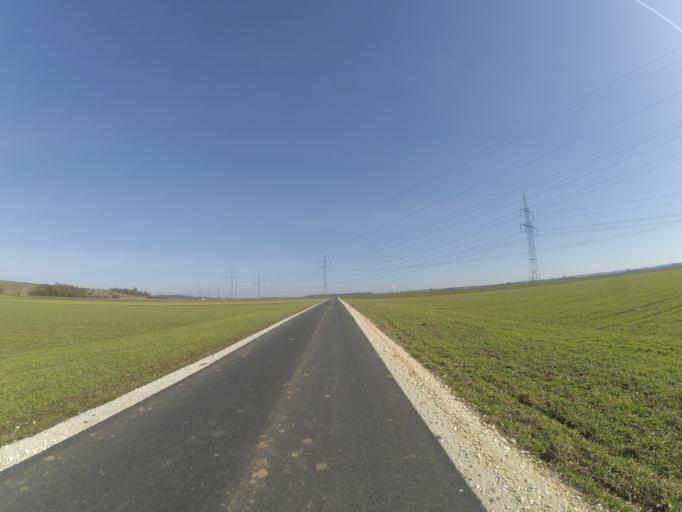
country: DE
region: Baden-Wuerttemberg
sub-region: Tuebingen Region
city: Asselfingen
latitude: 48.5146
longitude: 10.2124
